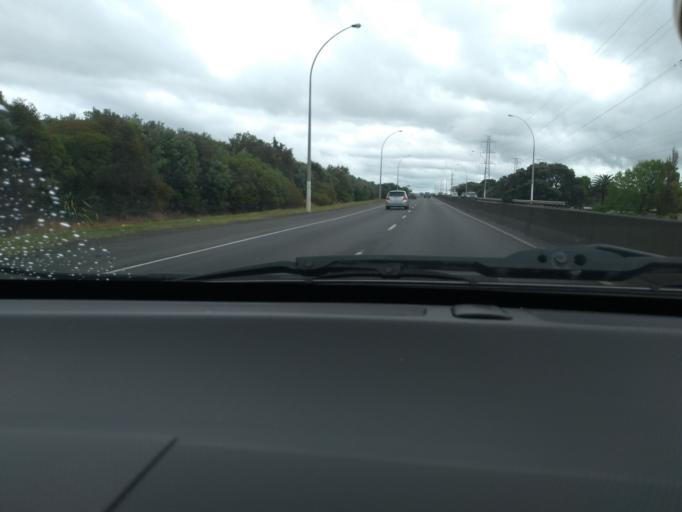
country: NZ
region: Auckland
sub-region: Auckland
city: Tamaki
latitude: -36.9143
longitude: 174.8639
